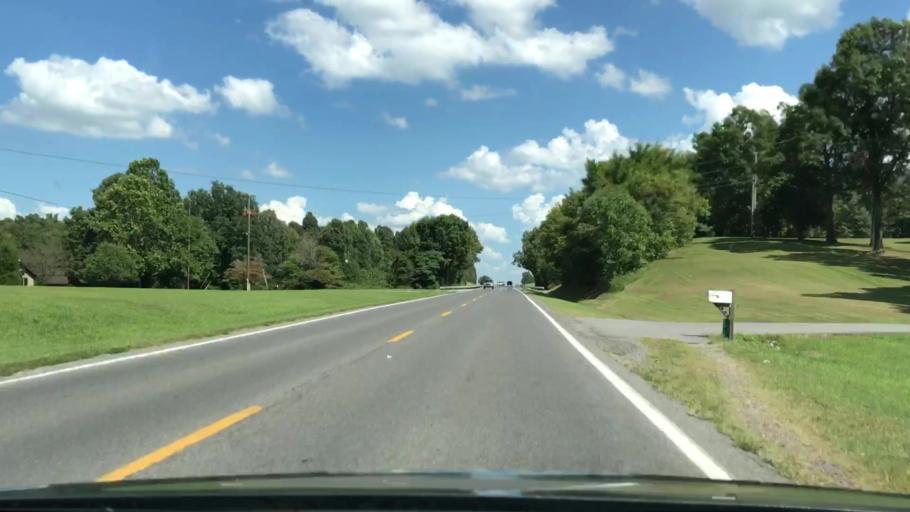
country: US
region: Kentucky
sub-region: Marshall County
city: Calvert City
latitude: 37.0044
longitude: -88.3664
